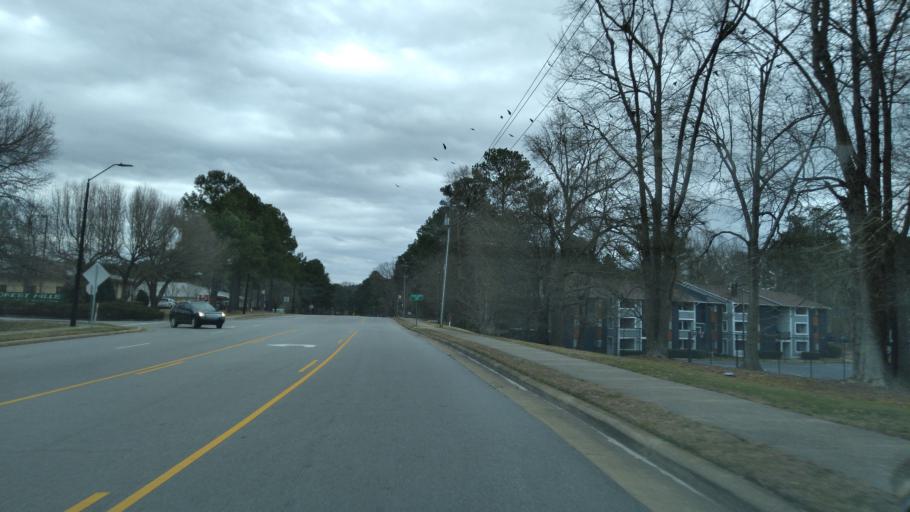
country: US
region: North Carolina
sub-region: Wake County
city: Garner
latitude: 35.7071
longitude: -78.6243
